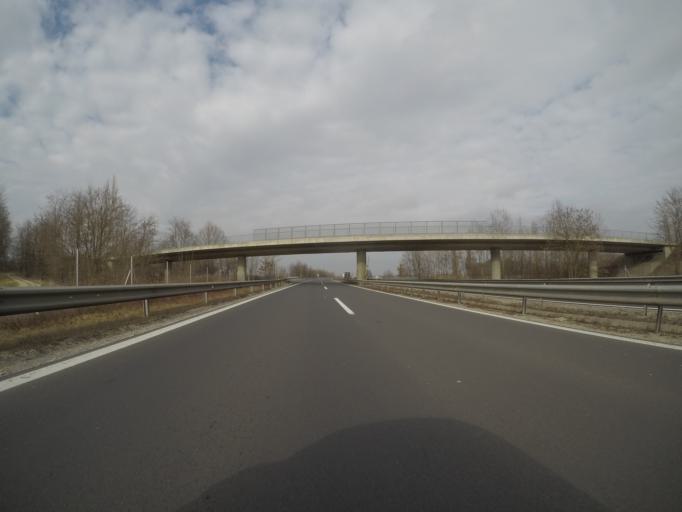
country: SI
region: Murska Sobota
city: Bakovci
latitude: 46.6173
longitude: 16.1316
